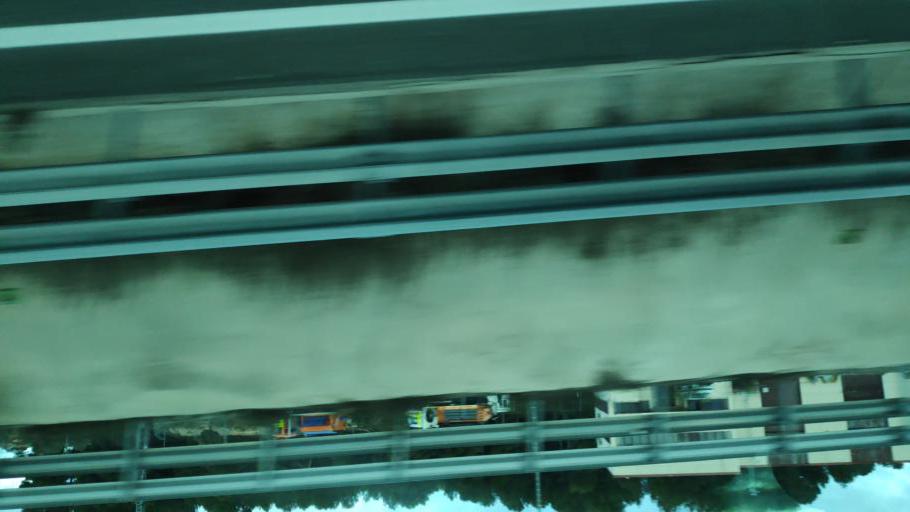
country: ES
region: Castille-La Mancha
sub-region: Provincia de Cuenca
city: Tarancon
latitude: 40.0158
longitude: -3.0320
